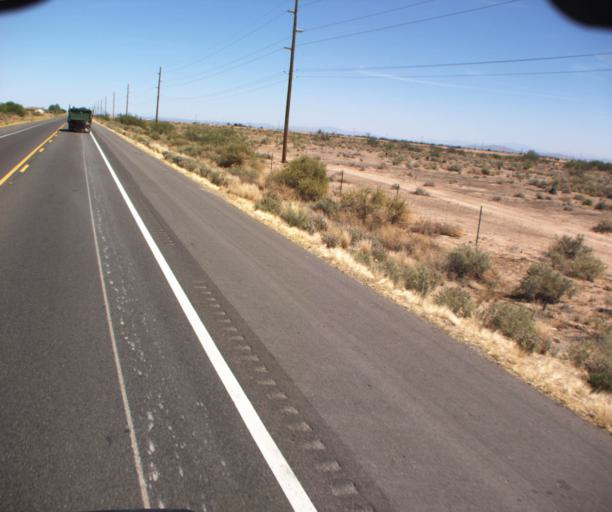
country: US
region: Arizona
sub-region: Pinal County
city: Blackwater
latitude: 33.0025
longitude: -111.5908
